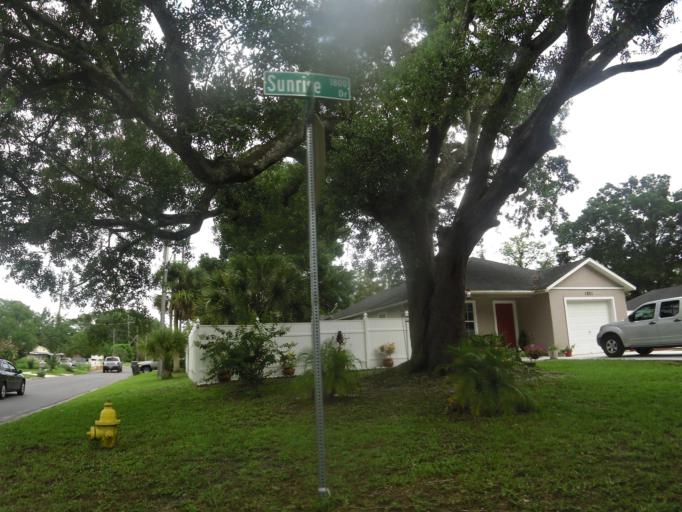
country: US
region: Florida
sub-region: Duval County
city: Jacksonville
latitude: 30.3189
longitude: -81.5368
